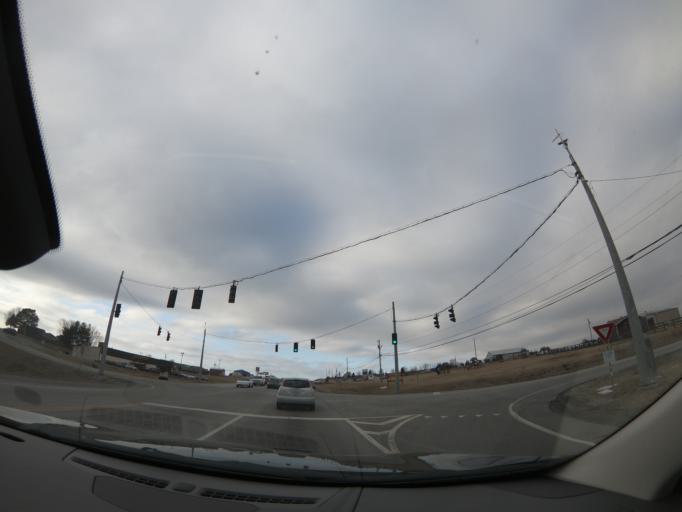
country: US
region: Kentucky
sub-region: Spencer County
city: Taylorsville
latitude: 38.0948
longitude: -85.3643
